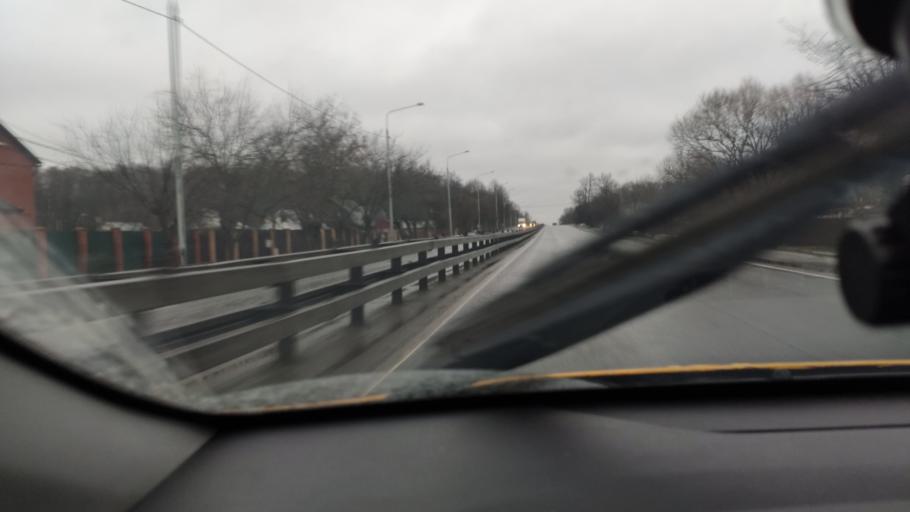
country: RU
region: Moskovskaya
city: Troitsk
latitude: 55.3265
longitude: 37.2721
